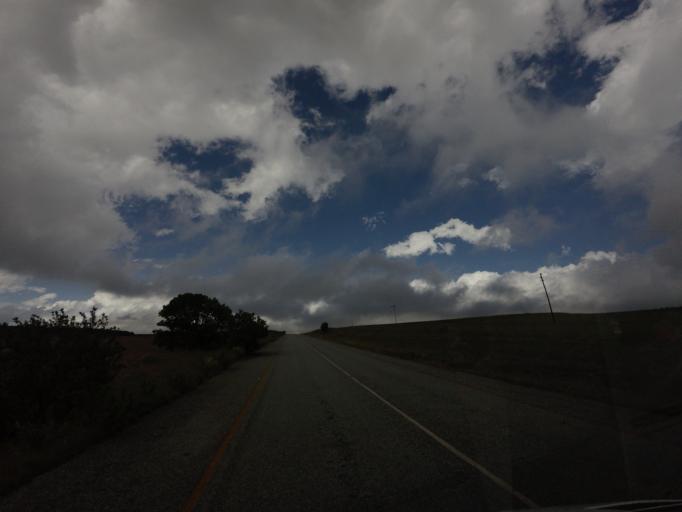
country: ZA
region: Mpumalanga
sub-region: Ehlanzeni District
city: Graksop
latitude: -24.8597
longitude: 30.8666
